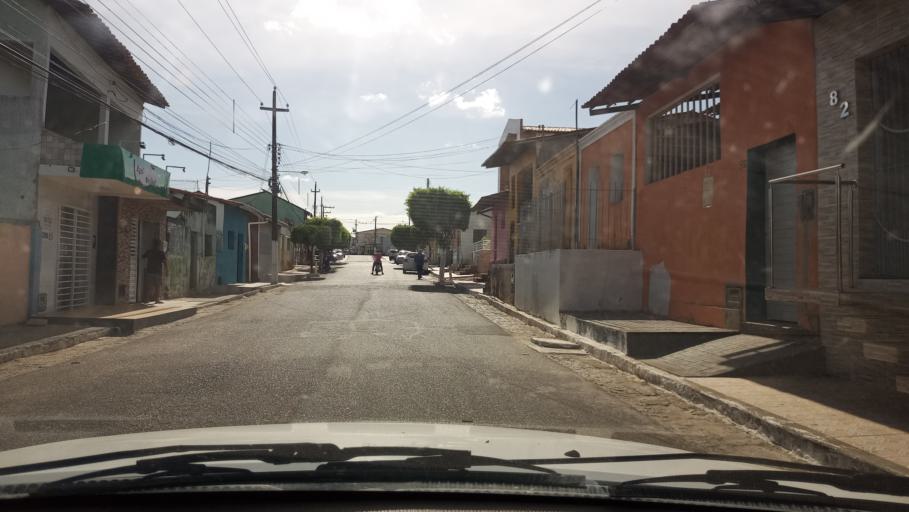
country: BR
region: Rio Grande do Norte
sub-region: Goianinha
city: Goianinha
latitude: -6.3318
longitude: -35.3087
